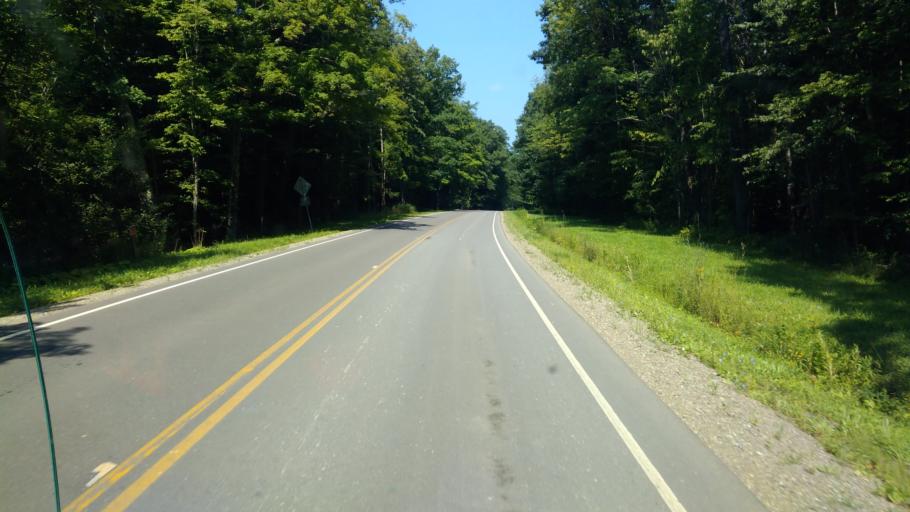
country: US
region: New York
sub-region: Allegany County
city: Belmont
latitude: 42.2633
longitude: -78.0403
